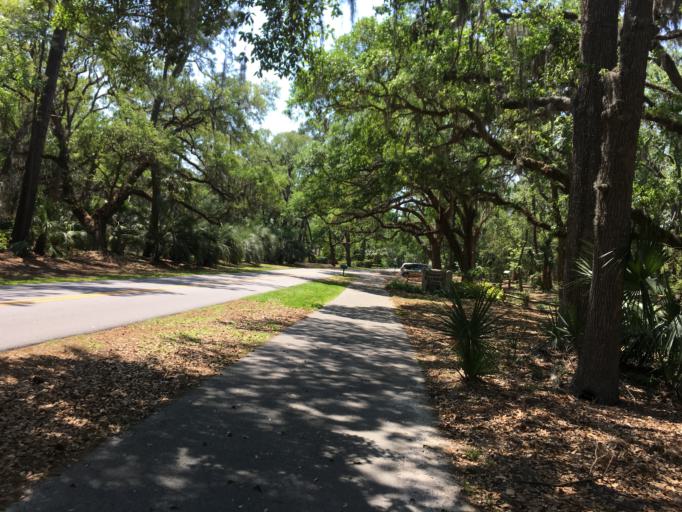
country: US
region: South Carolina
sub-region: Beaufort County
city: Hilton Head Island
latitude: 32.1293
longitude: -80.8128
